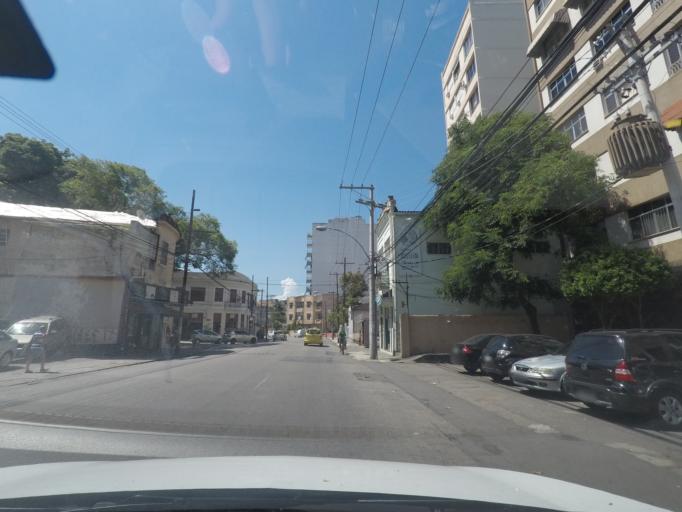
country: BR
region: Rio de Janeiro
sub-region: Rio De Janeiro
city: Rio de Janeiro
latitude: -22.9216
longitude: -43.2587
